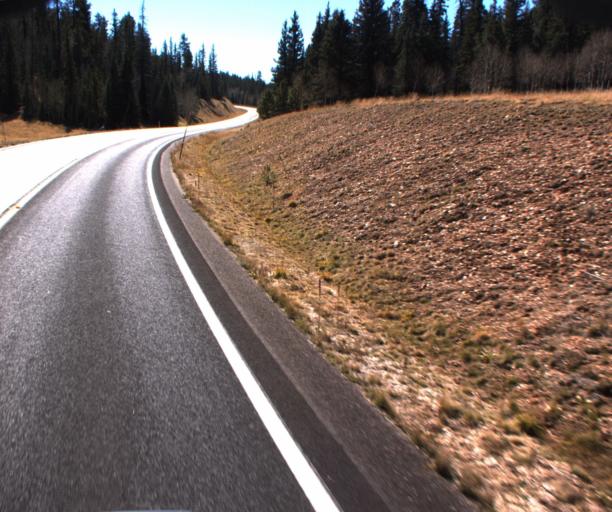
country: US
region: Arizona
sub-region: Coconino County
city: Grand Canyon
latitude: 36.5400
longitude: -112.1579
